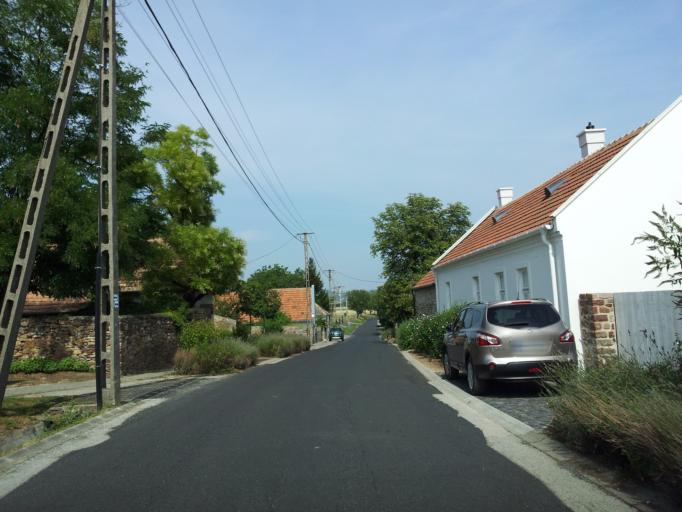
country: HU
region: Veszprem
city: Badacsonytomaj
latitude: 46.8513
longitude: 17.5601
